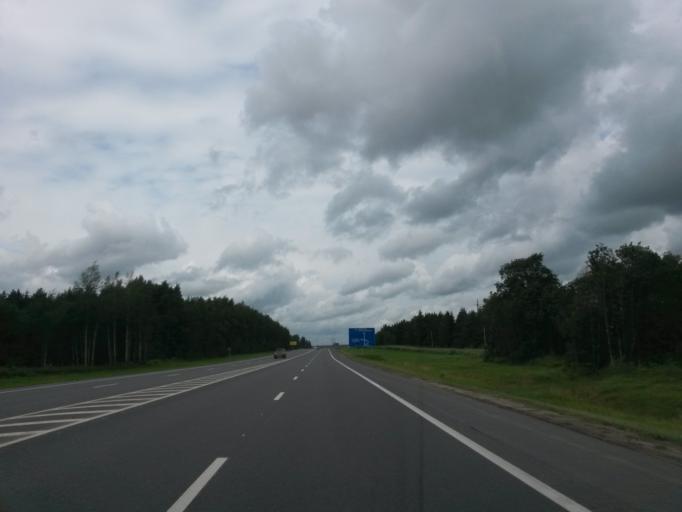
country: RU
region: Jaroslavl
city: Yaroslavl
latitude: 57.7293
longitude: 39.8986
